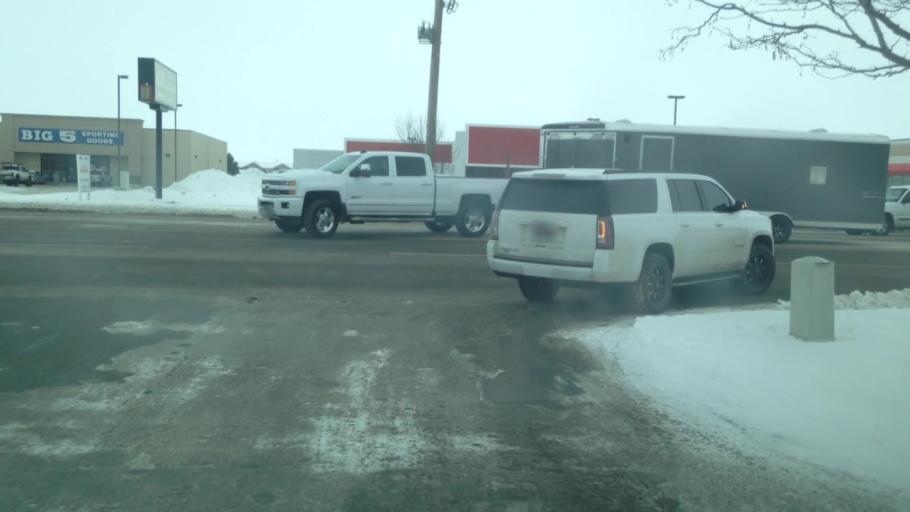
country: US
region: Idaho
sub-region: Madison County
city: Rexburg
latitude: 43.8394
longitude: -111.7783
